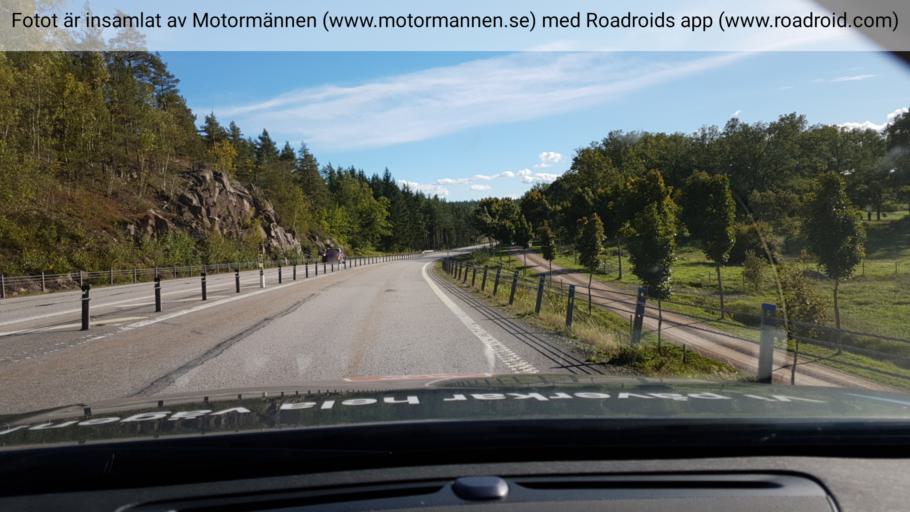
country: SE
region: Kalmar
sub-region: Vasterviks Kommun
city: Forserum
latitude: 58.0249
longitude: 16.5181
